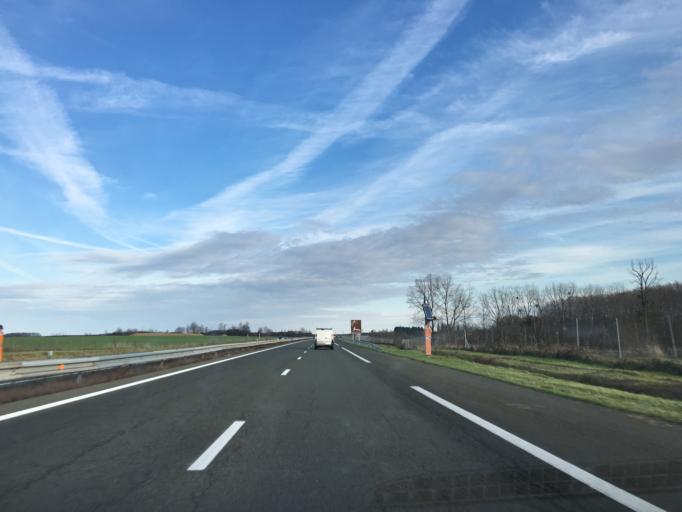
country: FR
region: Picardie
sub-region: Departement de l'Aisne
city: Essomes-sur-Marne
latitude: 49.0660
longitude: 3.3361
